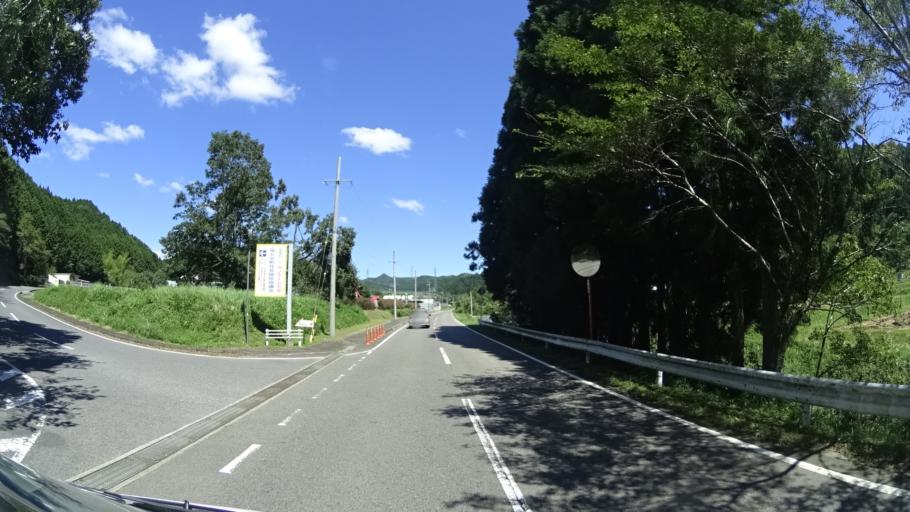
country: JP
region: Gifu
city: Minokamo
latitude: 35.5880
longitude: 137.0859
